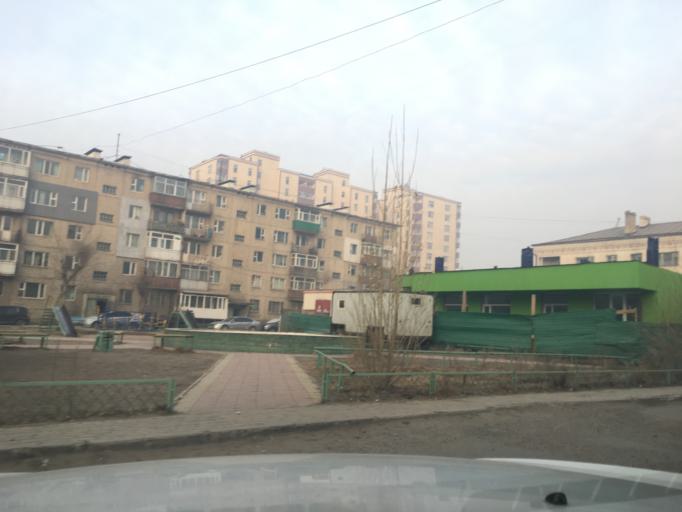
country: MN
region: Ulaanbaatar
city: Ulaanbaatar
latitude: 47.9165
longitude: 106.8139
